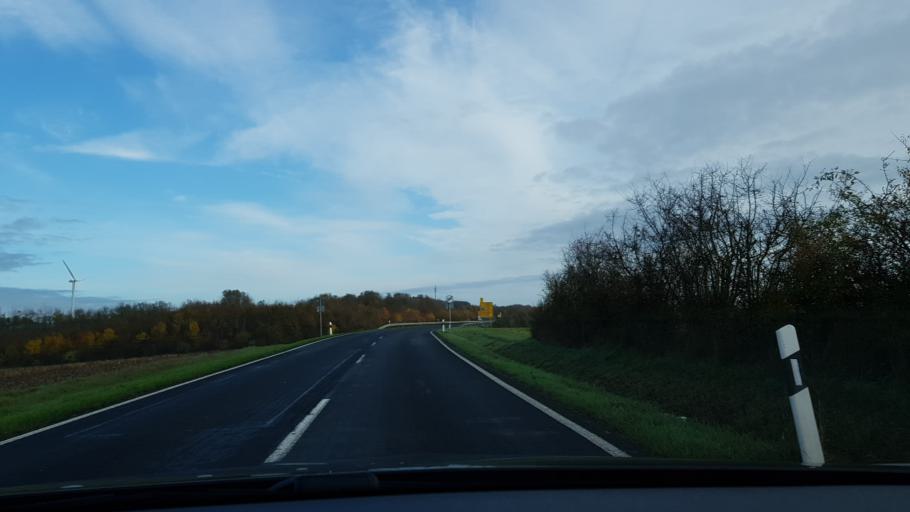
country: DE
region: Rheinland-Pfalz
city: Bitburg
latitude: 49.9907
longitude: 6.5300
